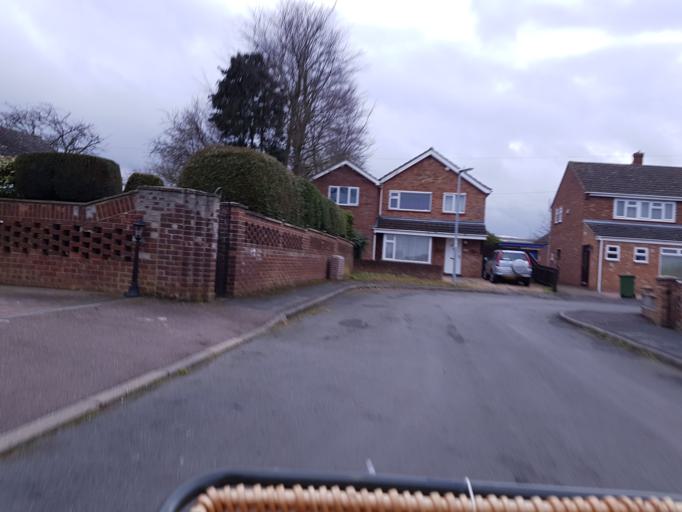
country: GB
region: England
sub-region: Cambridgeshire
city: Fulbourn
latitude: 52.1963
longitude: 0.1768
